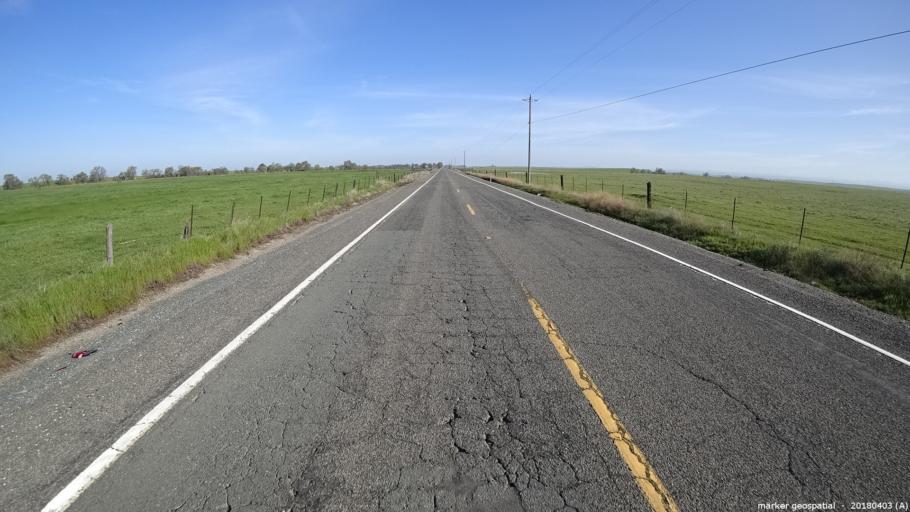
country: US
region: California
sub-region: Sacramento County
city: Clay
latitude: 38.3775
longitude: -121.1685
